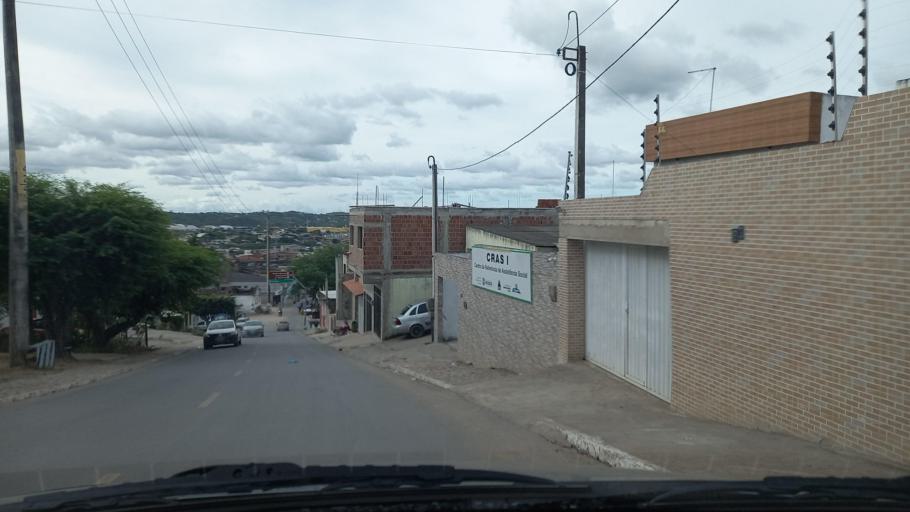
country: BR
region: Pernambuco
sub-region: Gravata
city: Gravata
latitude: -8.2118
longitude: -35.5719
